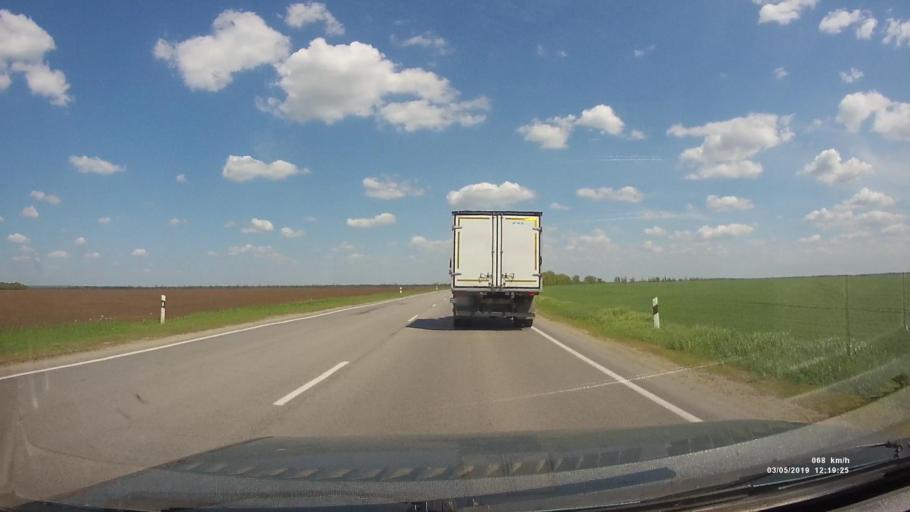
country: RU
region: Rostov
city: Melikhovskaya
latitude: 47.4003
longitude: 40.6077
